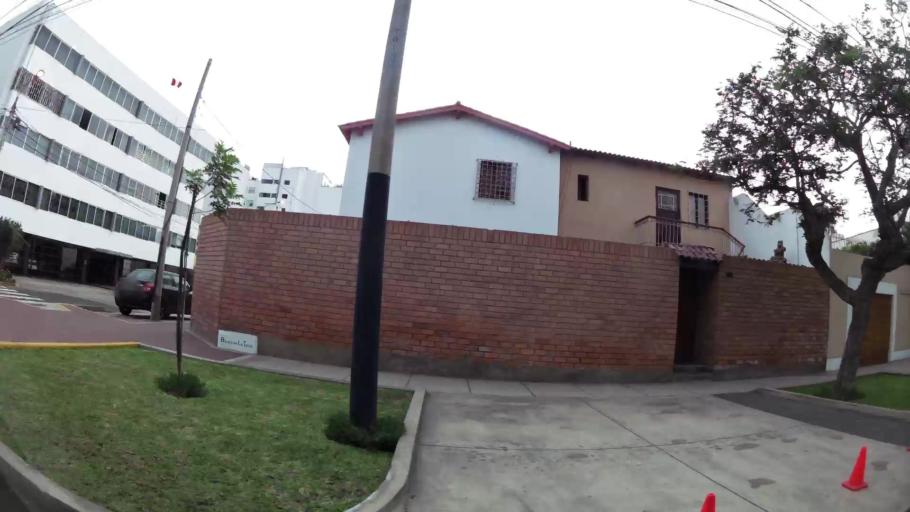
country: PE
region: Lima
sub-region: Lima
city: San Isidro
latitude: -12.1025
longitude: -77.0568
